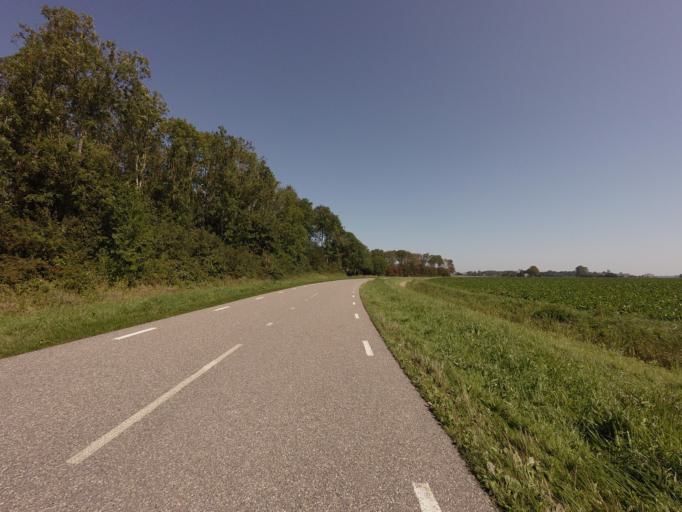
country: NL
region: Friesland
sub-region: Gemeente Dongeradeel
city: Ternaard
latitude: 53.3667
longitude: 5.9820
